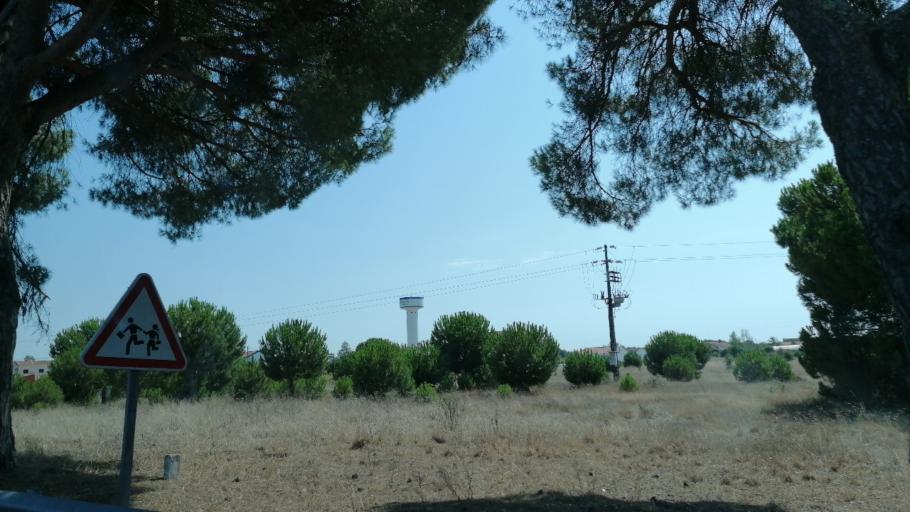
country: PT
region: Santarem
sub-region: Benavente
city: Poceirao
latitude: 38.7476
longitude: -8.6649
